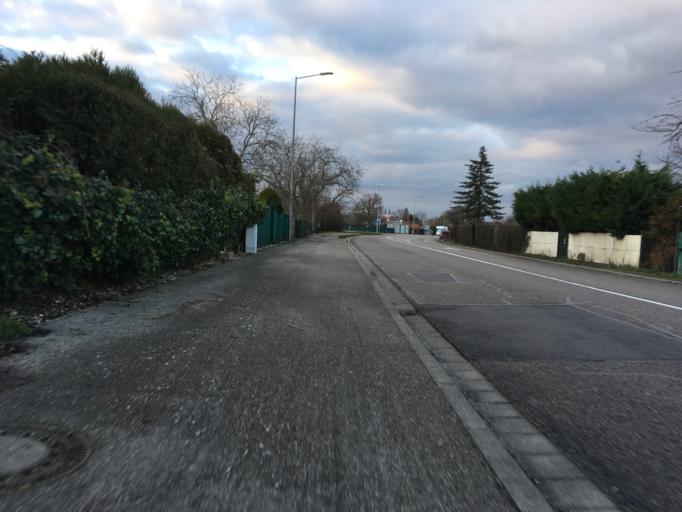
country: DE
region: Rheinland-Pfalz
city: Speyer
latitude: 49.3004
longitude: 8.4505
